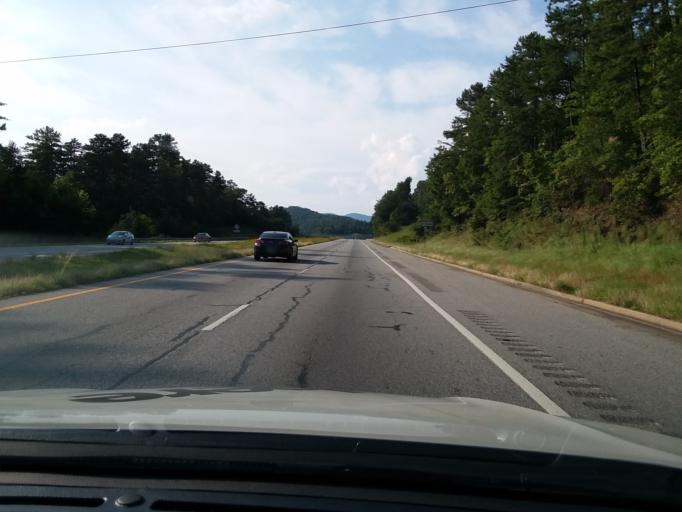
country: US
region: Georgia
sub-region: Rabun County
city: Clayton
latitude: 34.8218
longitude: -83.4235
